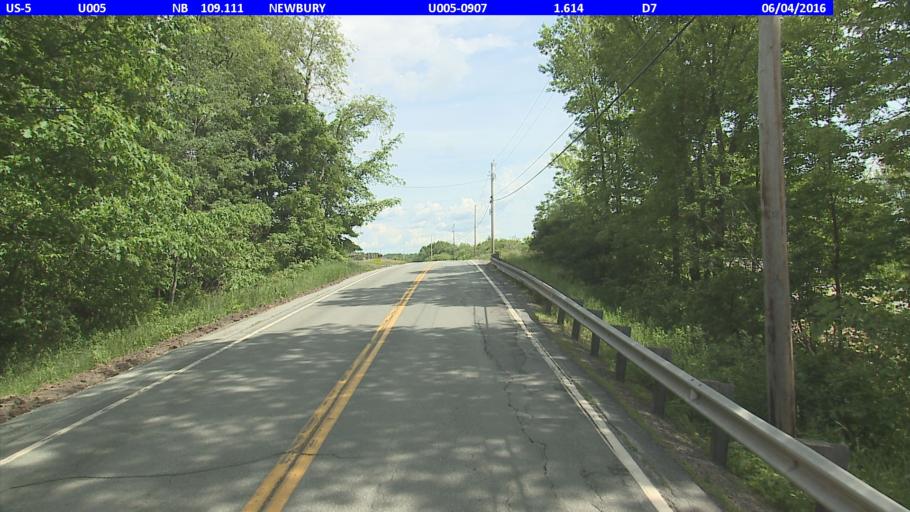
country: US
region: New Hampshire
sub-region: Grafton County
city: Haverhill
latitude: 44.0523
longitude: -72.0735
